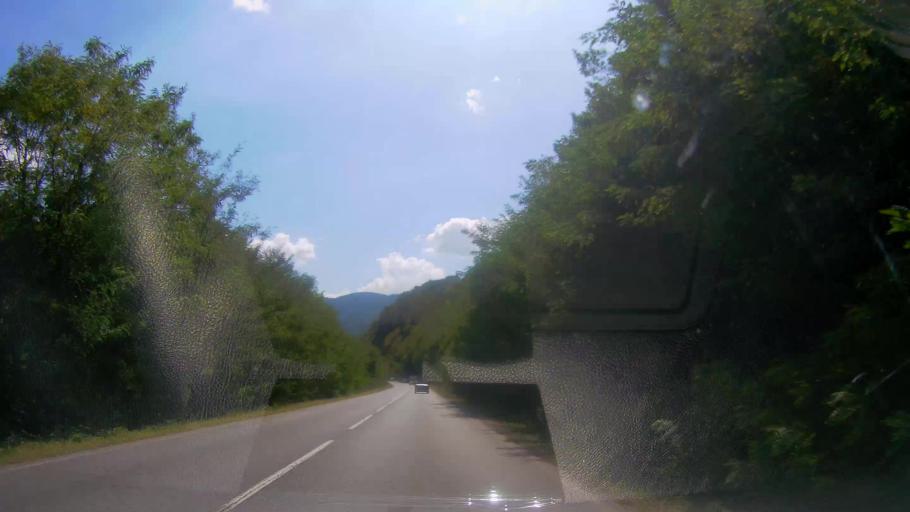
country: BG
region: Stara Zagora
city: Gurkovo
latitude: 42.7269
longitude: 25.7124
